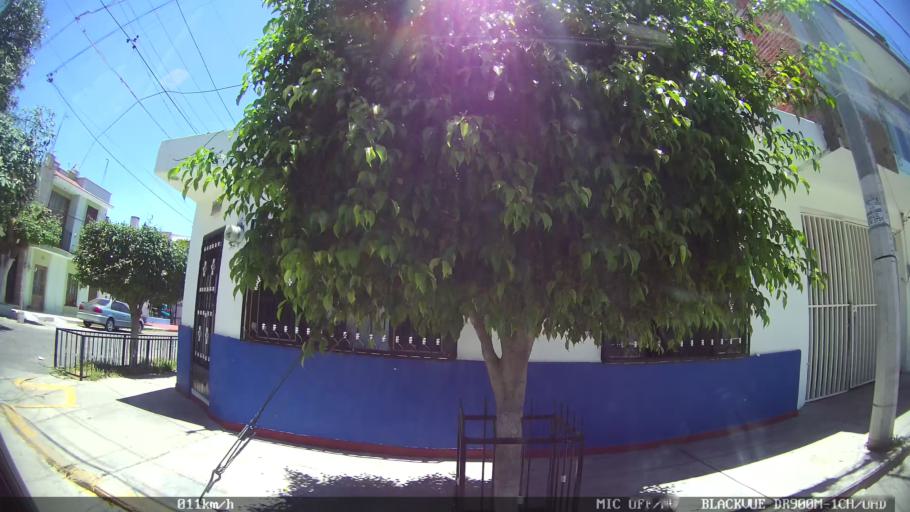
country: MX
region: Jalisco
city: Tlaquepaque
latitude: 20.6711
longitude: -103.2867
